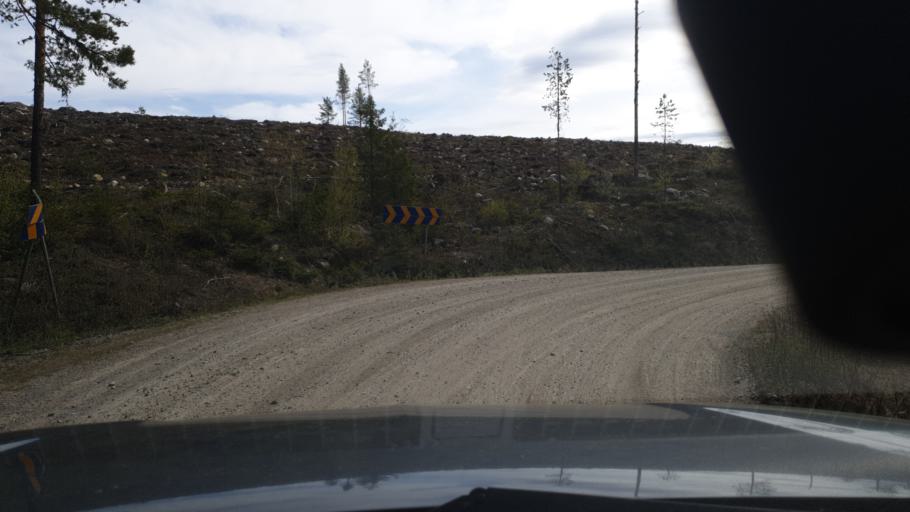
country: SE
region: Vaesternorrland
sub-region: Ange Kommun
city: Ange
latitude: 62.2587
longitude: 15.4842
